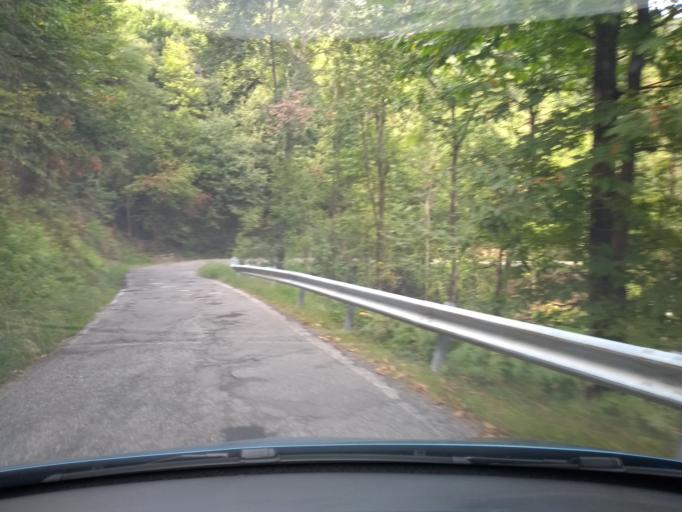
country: IT
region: Piedmont
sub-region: Provincia di Torino
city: Corio
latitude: 45.3072
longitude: 7.5135
